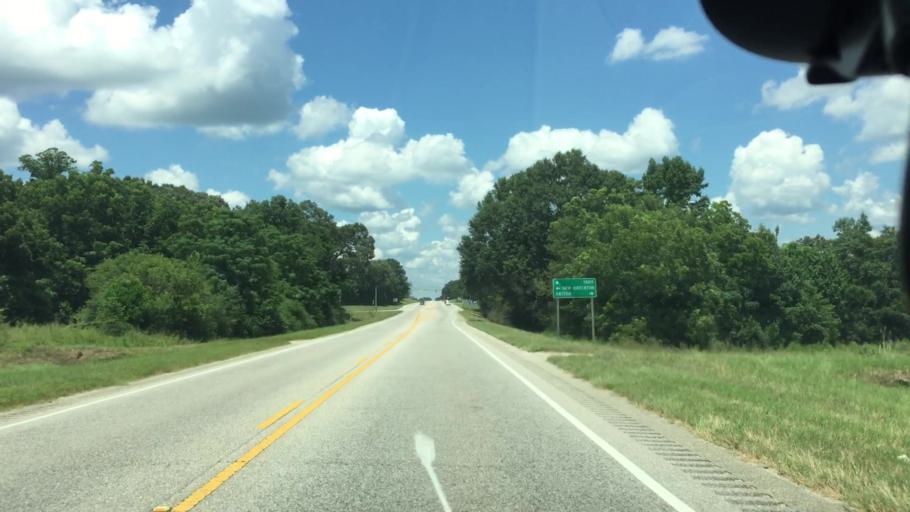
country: US
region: Alabama
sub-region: Coffee County
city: New Brockton
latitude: 31.4234
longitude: -85.8873
